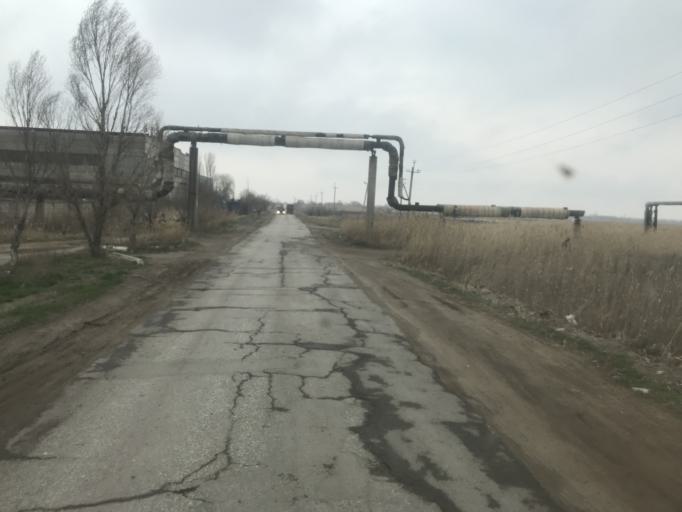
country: RU
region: Volgograd
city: Svetlyy Yar
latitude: 48.5255
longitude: 44.6156
